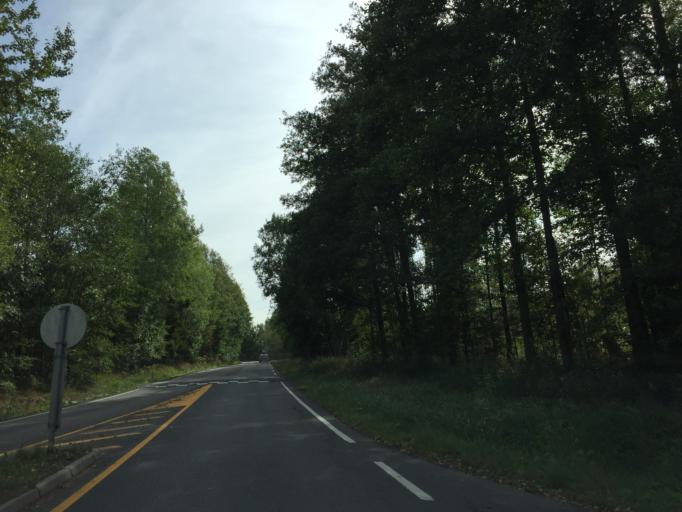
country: NO
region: Ostfold
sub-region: Moss
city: Moss
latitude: 59.4882
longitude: 10.6932
